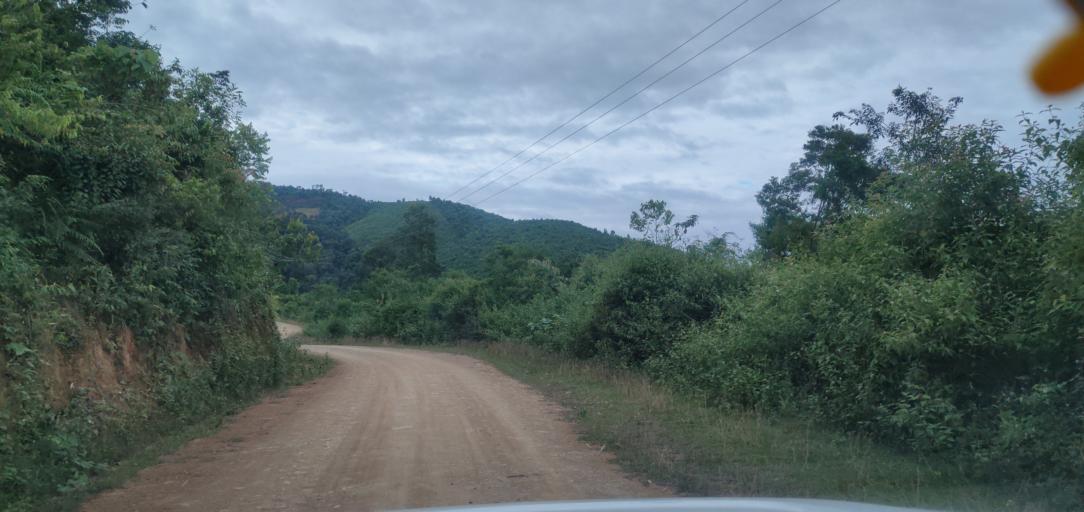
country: LA
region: Phongsali
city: Khoa
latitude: 21.1905
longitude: 102.3002
